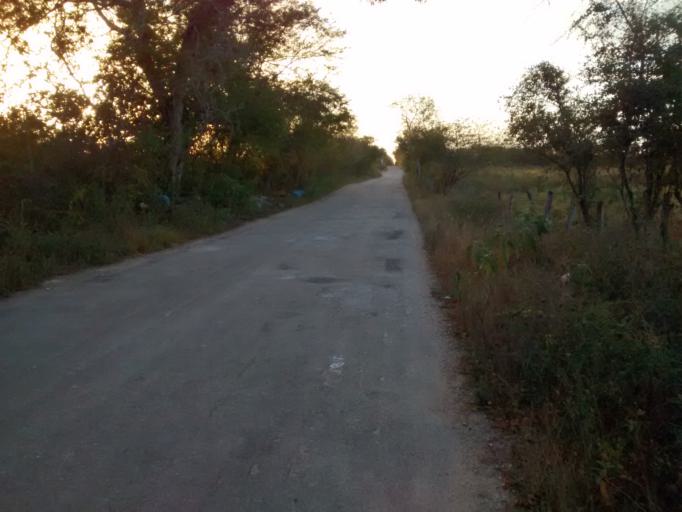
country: MX
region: Yucatan
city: Valladolid
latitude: 20.6828
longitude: -88.1708
